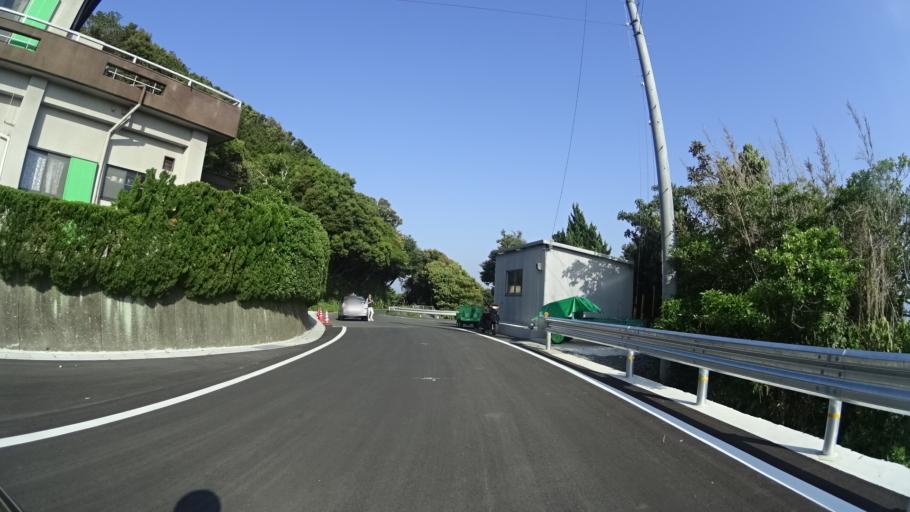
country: JP
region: Oita
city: Tsukumiura
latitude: 33.3475
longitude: 132.0254
